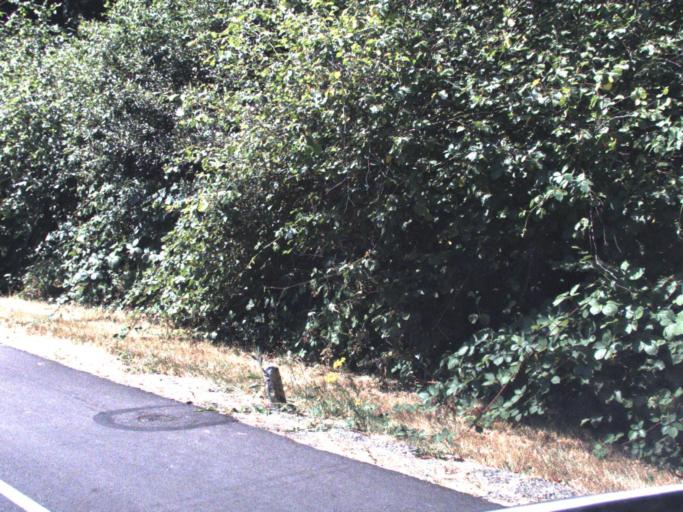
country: US
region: Washington
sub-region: King County
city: Redmond
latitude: 47.7009
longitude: -122.1320
